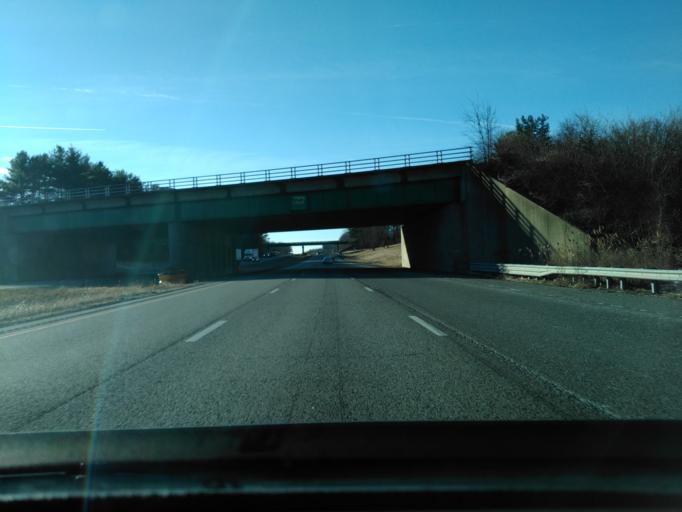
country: US
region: Illinois
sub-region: Franklin County
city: West Frankfort
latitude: 37.8945
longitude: -88.9459
